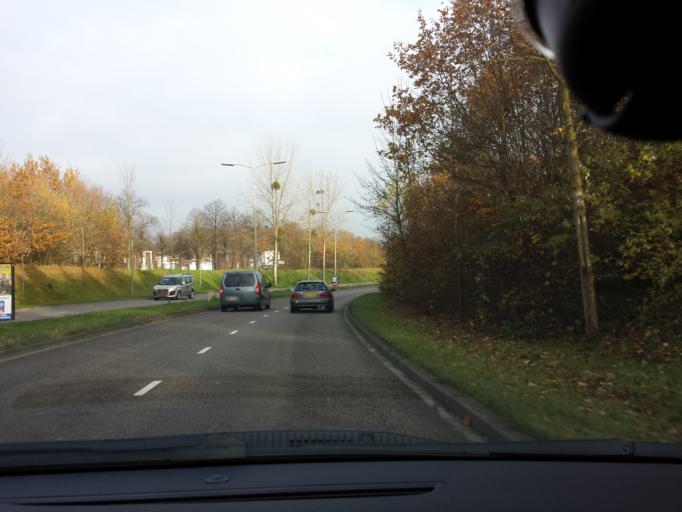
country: NL
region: Limburg
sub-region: Gemeente Heerlen
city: Heerlen
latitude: 50.9025
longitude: 5.9651
